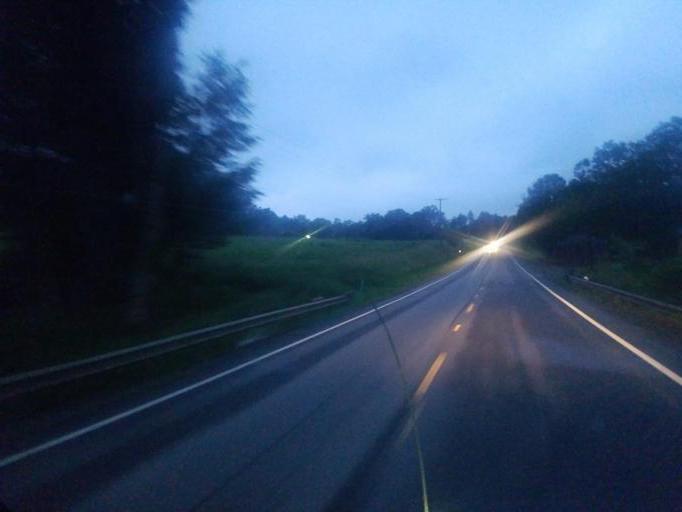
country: US
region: Ohio
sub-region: Carroll County
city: Carrollton
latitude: 40.5398
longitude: -81.0301
